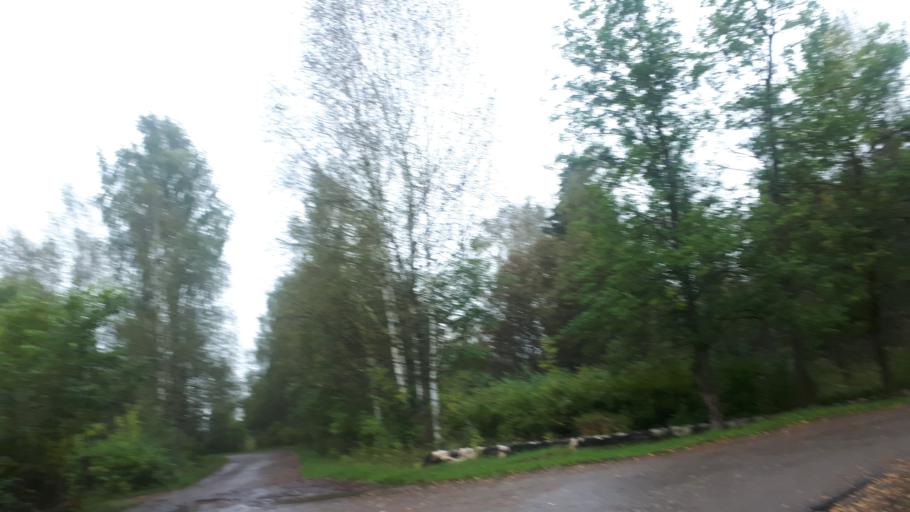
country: RU
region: Jaroslavl
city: Konstantinovskiy
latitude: 57.8260
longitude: 39.5854
